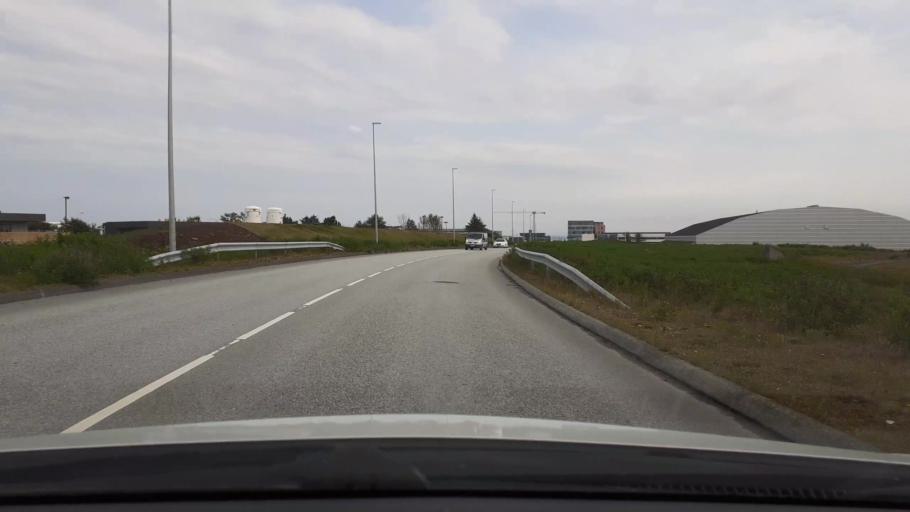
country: IS
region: Southern Peninsula
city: Reykjanesbaer
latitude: 63.9945
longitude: -22.5645
